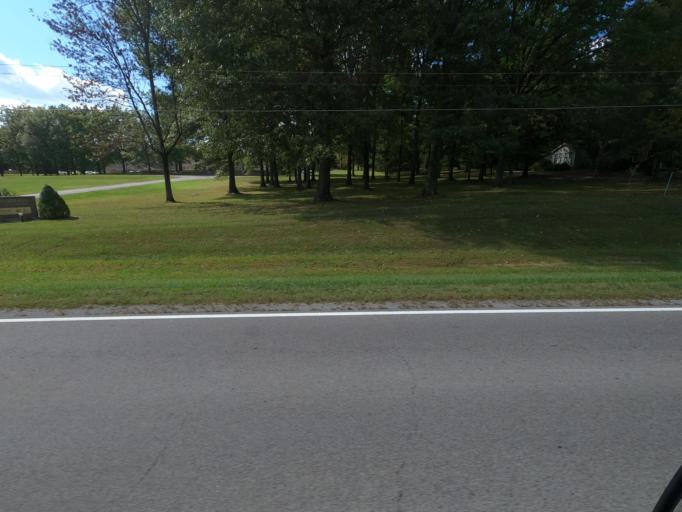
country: US
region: Illinois
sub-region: Johnson County
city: Vienna
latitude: 37.4274
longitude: -88.8930
